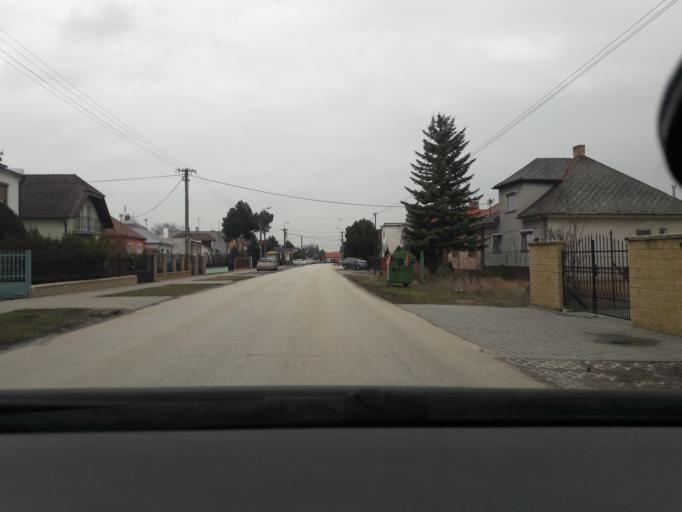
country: SK
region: Bratislavsky
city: Senec
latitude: 48.2998
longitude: 17.4512
